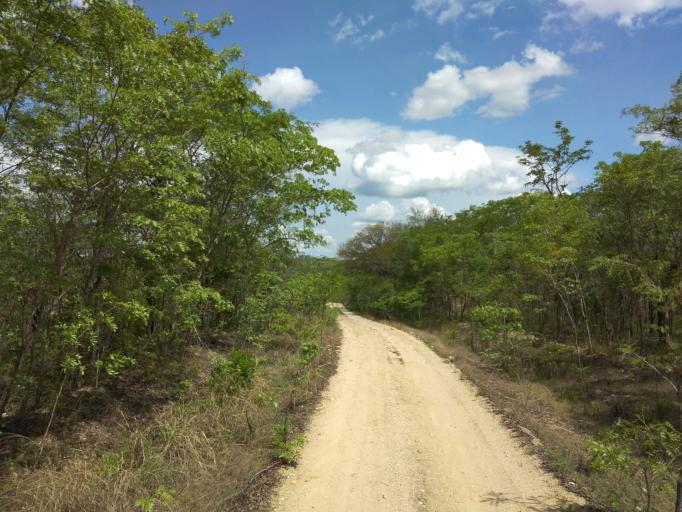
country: ZM
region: Central
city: Mkushi
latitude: -14.1243
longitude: 30.0194
